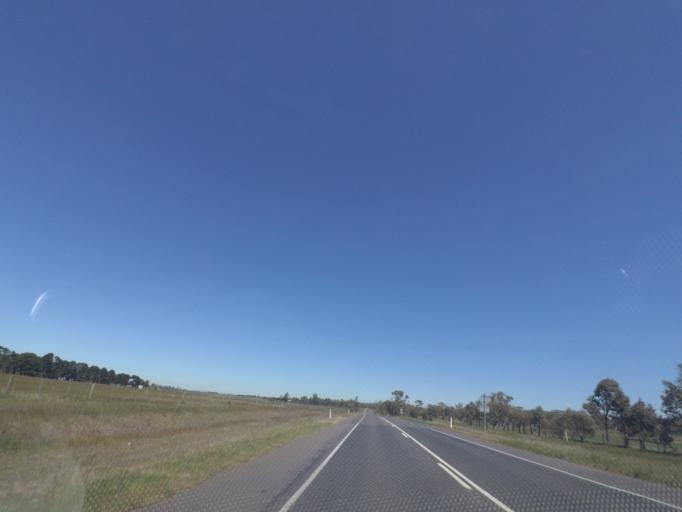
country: AU
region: Victoria
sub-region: Hume
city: Craigieburn
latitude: -37.2900
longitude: 144.8864
